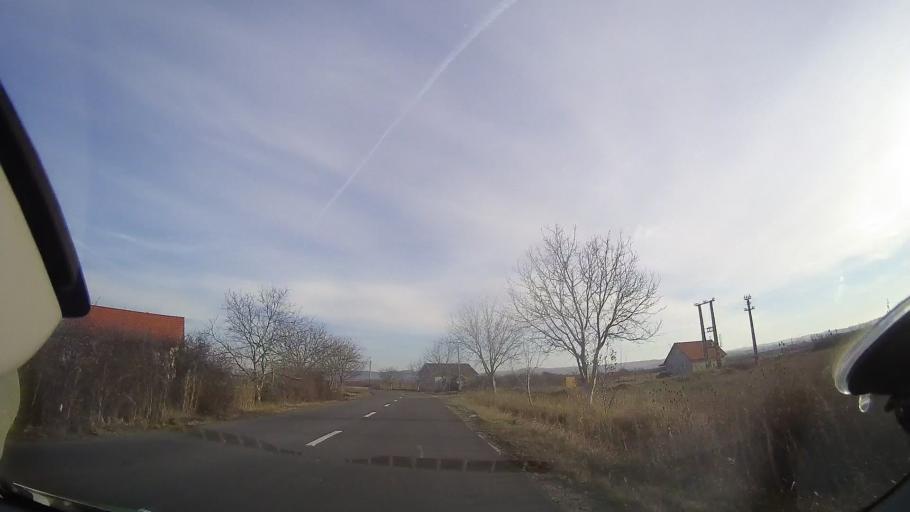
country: RO
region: Bihor
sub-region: Comuna Tileagd
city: Tileagd
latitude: 47.0647
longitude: 22.2233
